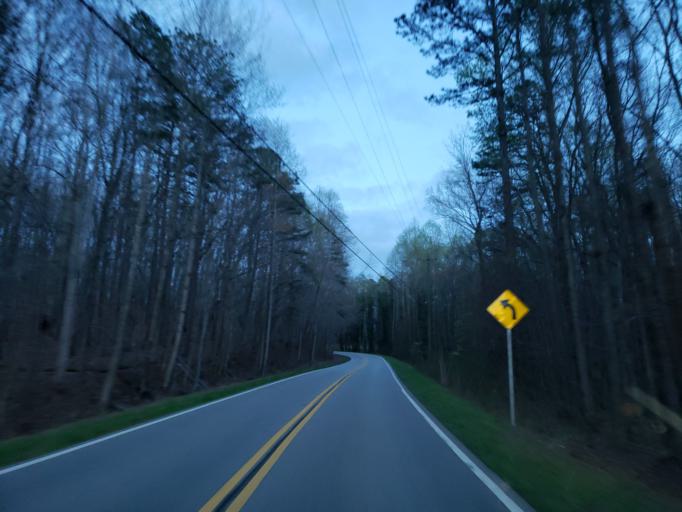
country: US
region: Georgia
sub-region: Paulding County
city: Dallas
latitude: 34.0155
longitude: -84.8707
